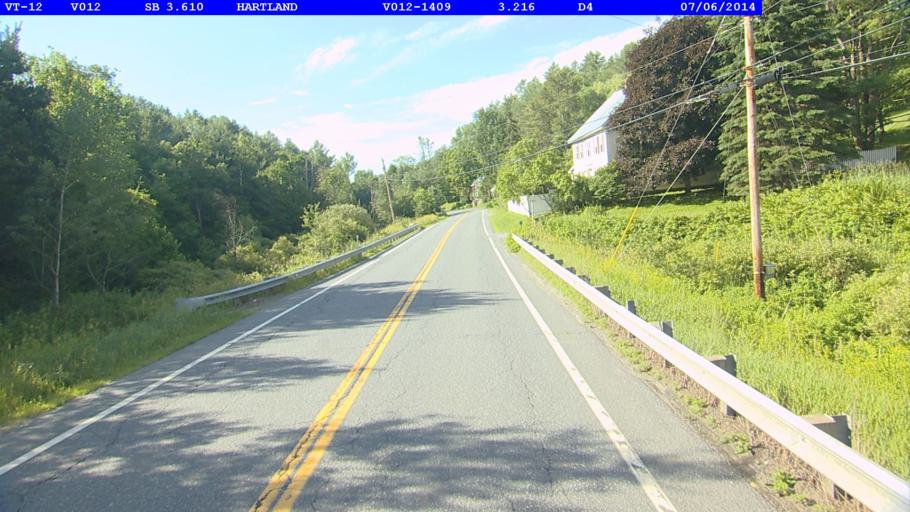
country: US
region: Vermont
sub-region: Windsor County
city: Woodstock
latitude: 43.5652
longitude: -72.4436
